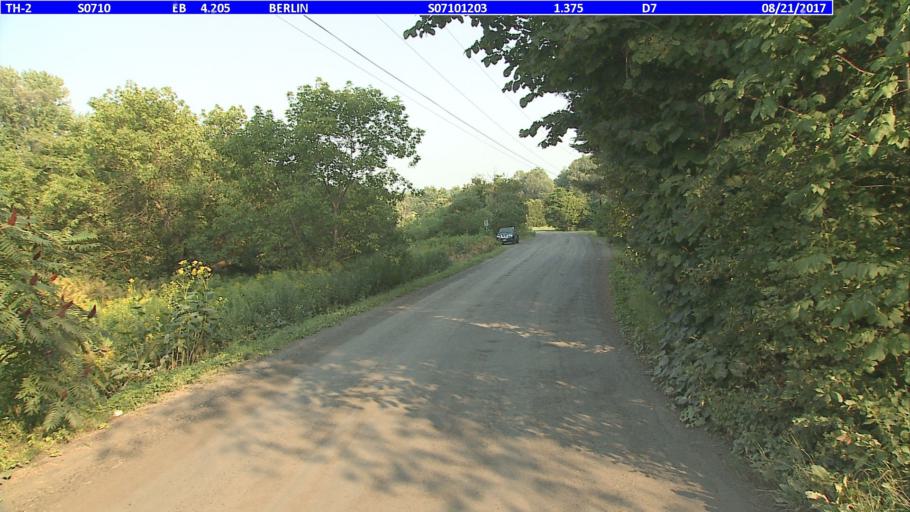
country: US
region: Vermont
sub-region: Washington County
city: Montpelier
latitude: 44.2594
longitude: -72.6174
